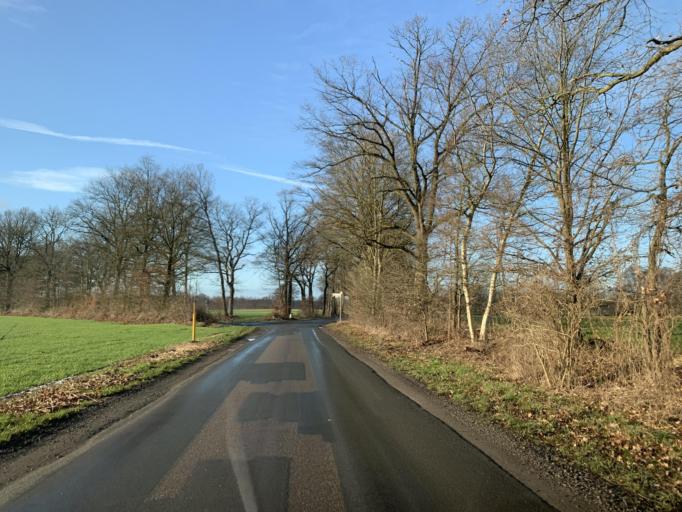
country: DE
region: North Rhine-Westphalia
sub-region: Regierungsbezirk Munster
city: Dulmen
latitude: 51.8066
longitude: 7.2969
